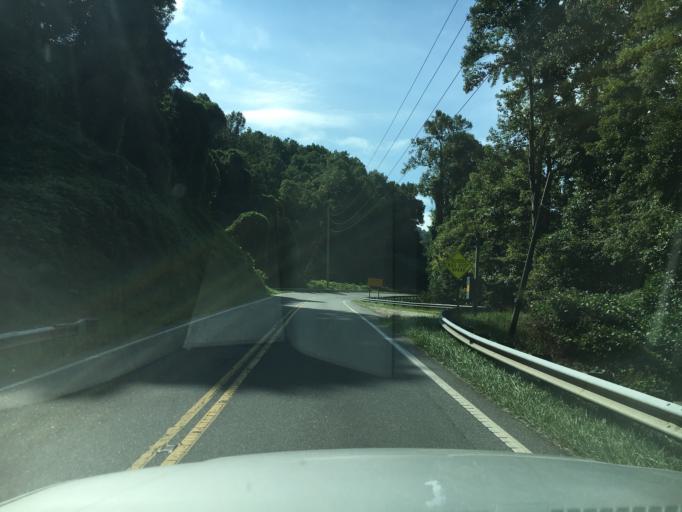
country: US
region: North Carolina
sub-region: Swain County
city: Bryson City
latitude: 35.3619
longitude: -83.5539
